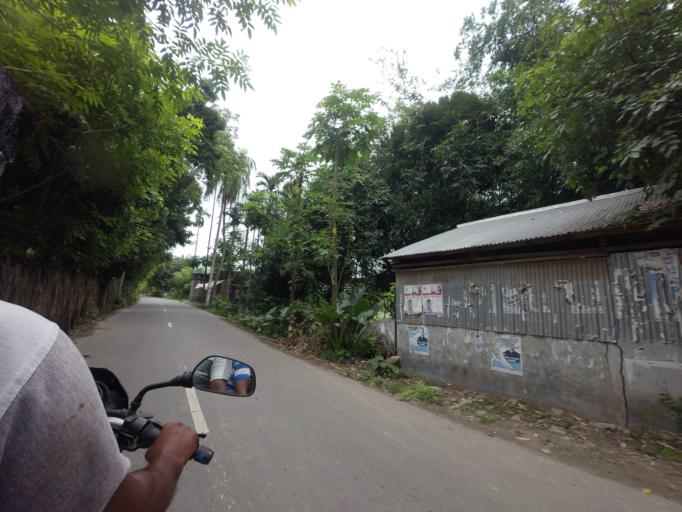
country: BD
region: Khulna
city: Kalia
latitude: 23.1743
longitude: 89.6467
